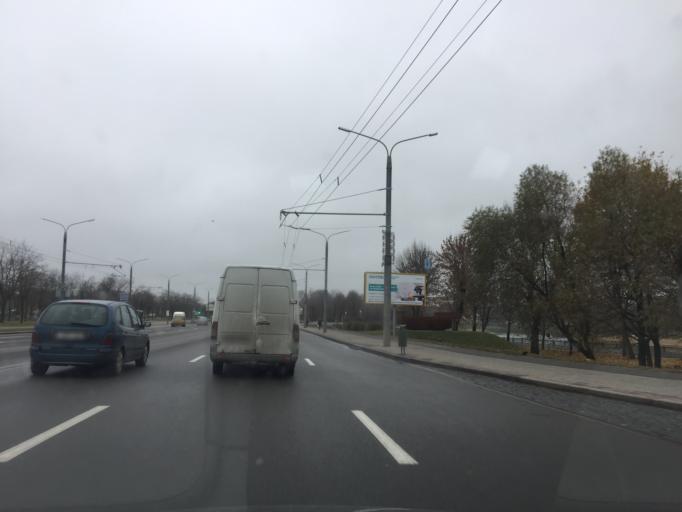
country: BY
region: Mogilev
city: Mahilyow
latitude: 53.8852
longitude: 30.3330
